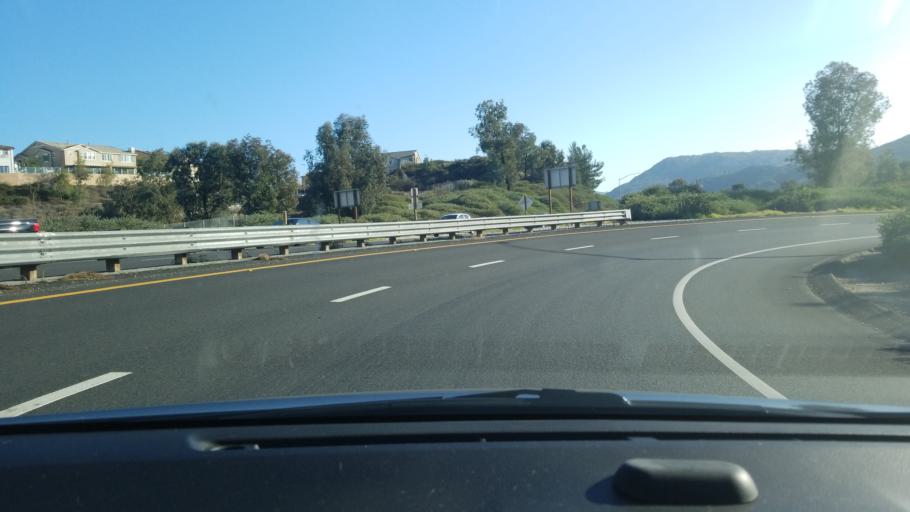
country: US
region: California
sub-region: Riverside County
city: Temecula
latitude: 33.5009
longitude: -117.1501
